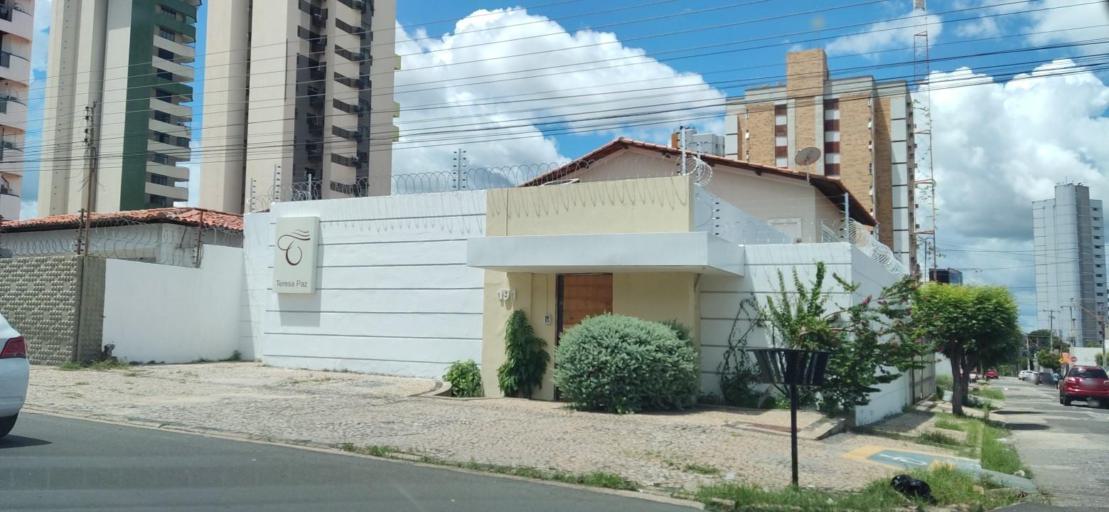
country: BR
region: Piaui
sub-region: Teresina
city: Teresina
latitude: -5.0864
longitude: -42.7988
